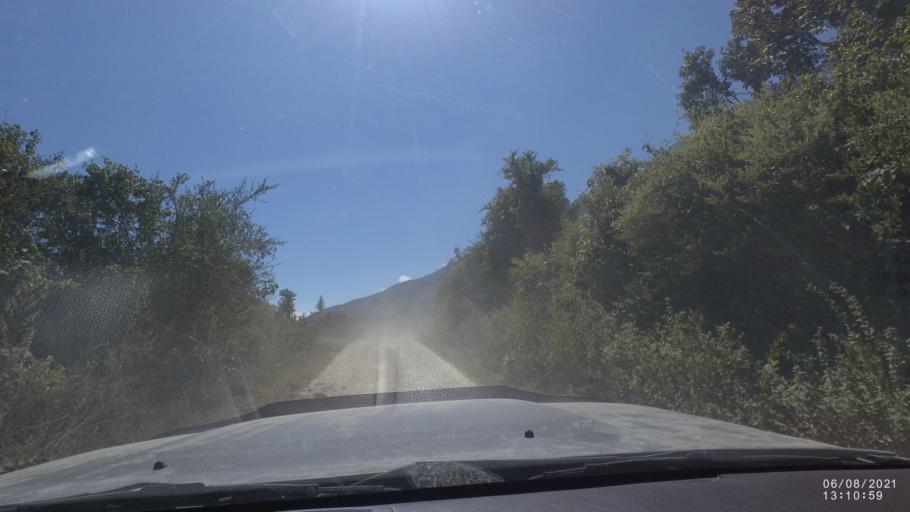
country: BO
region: La Paz
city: Quime
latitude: -16.7225
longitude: -66.7058
